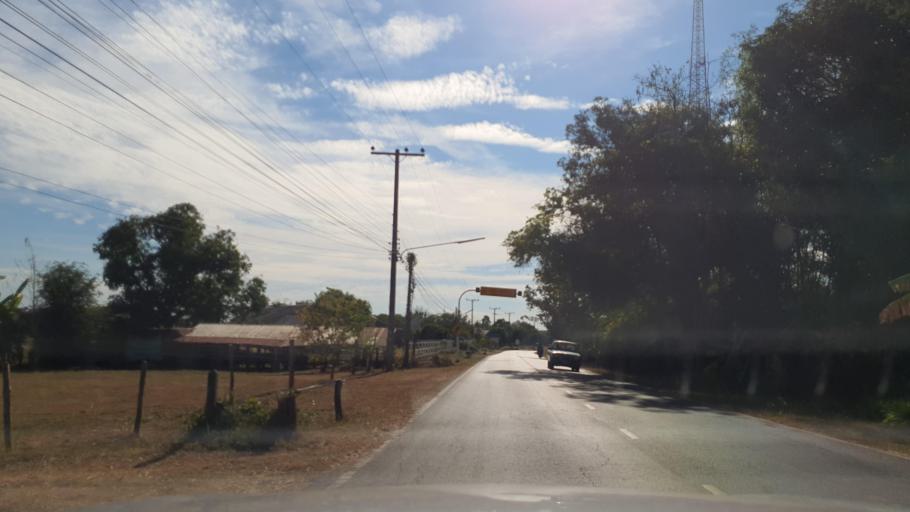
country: TH
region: Kalasin
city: Kuchinarai
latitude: 16.5448
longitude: 104.0938
